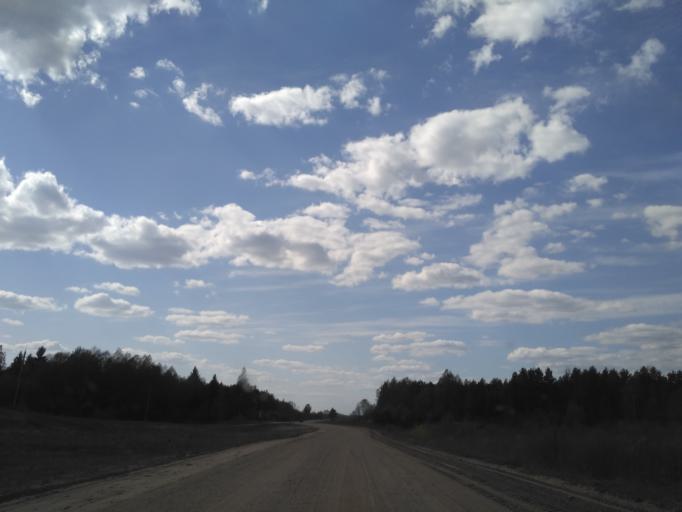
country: BY
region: Minsk
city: Narach
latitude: 54.9927
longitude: 26.5718
